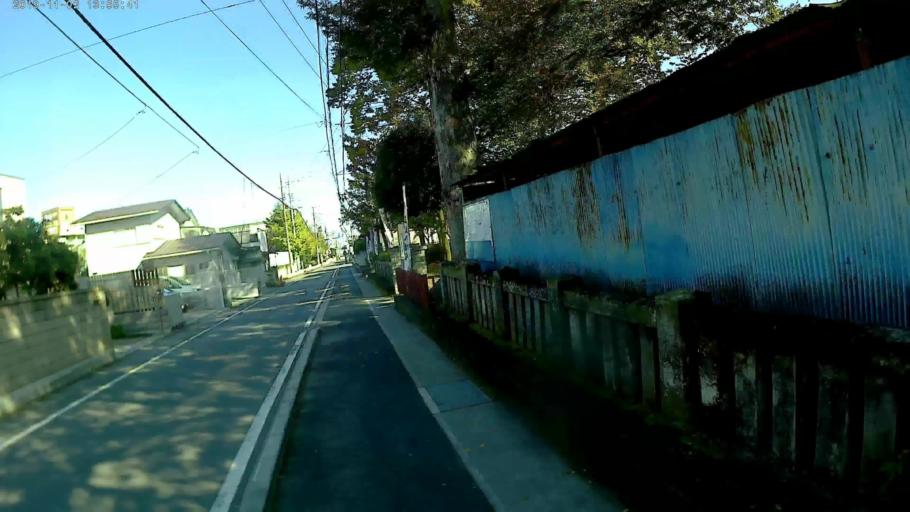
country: JP
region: Gunma
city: Takasaki
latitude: 36.3340
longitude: 138.9739
